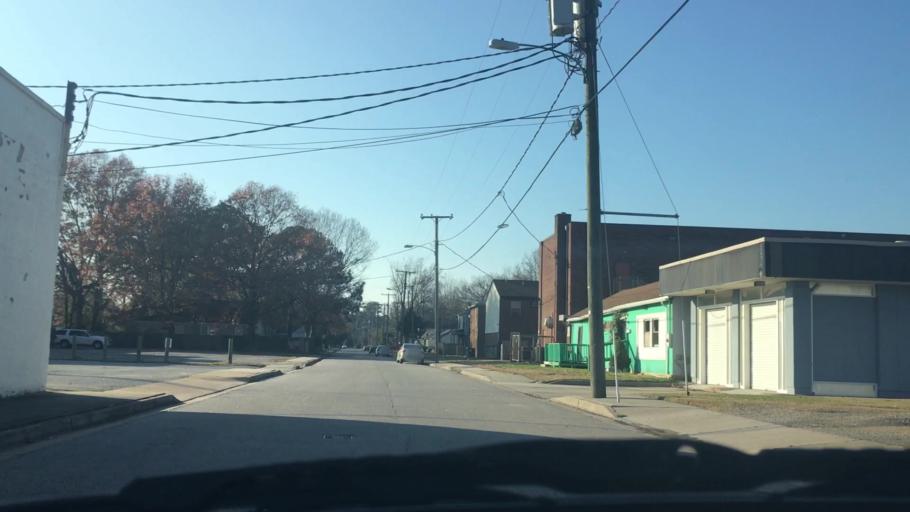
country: US
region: Virginia
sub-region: City of Norfolk
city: Norfolk
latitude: 36.8905
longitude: -76.2391
